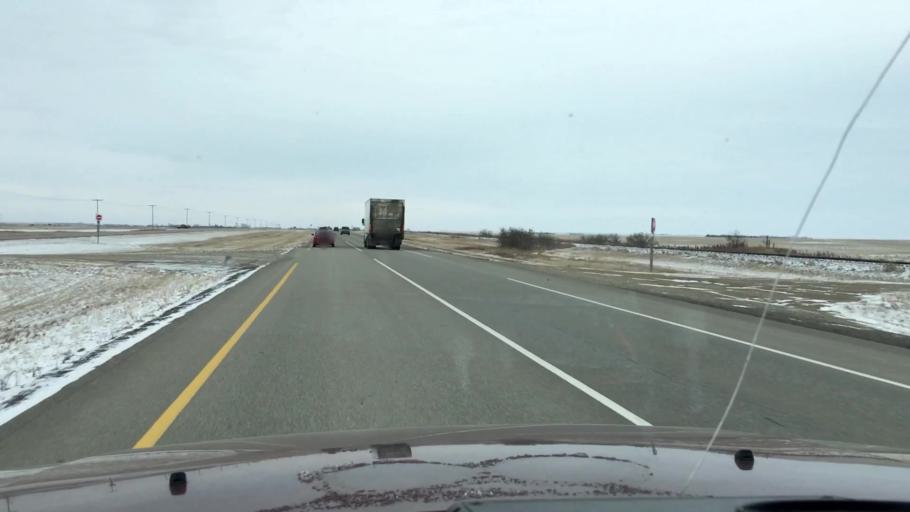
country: CA
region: Saskatchewan
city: Watrous
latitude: 51.1834
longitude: -105.9420
